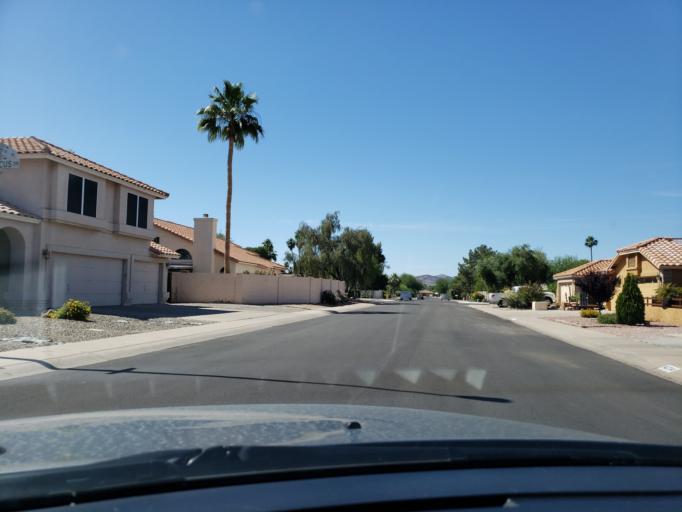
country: US
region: Arizona
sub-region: Maricopa County
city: Paradise Valley
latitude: 33.6158
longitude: -111.9578
